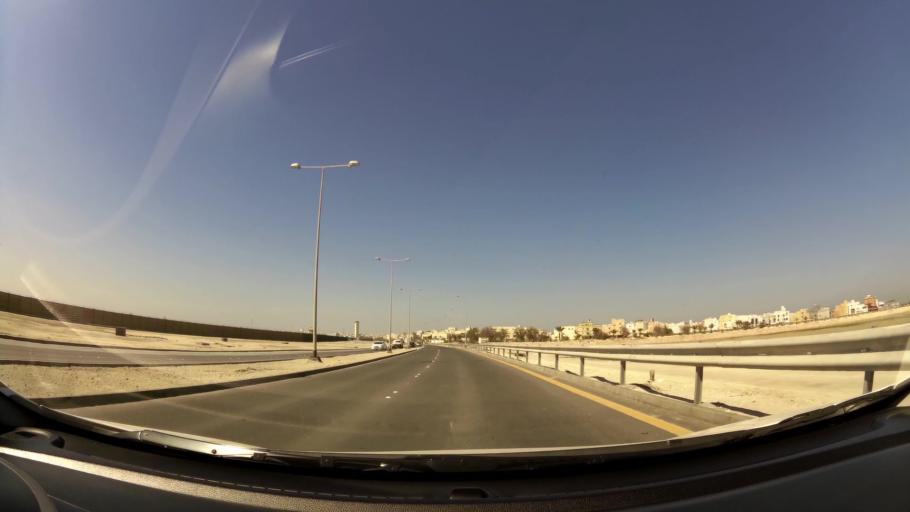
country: BH
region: Muharraq
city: Al Hadd
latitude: 26.2603
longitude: 50.6559
